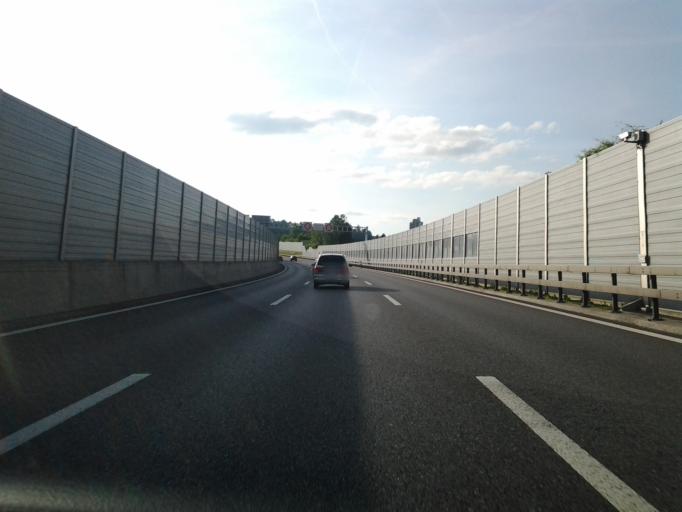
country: CH
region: Lucerne
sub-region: Hochdorf District
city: Emmen
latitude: 47.0794
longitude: 8.2901
